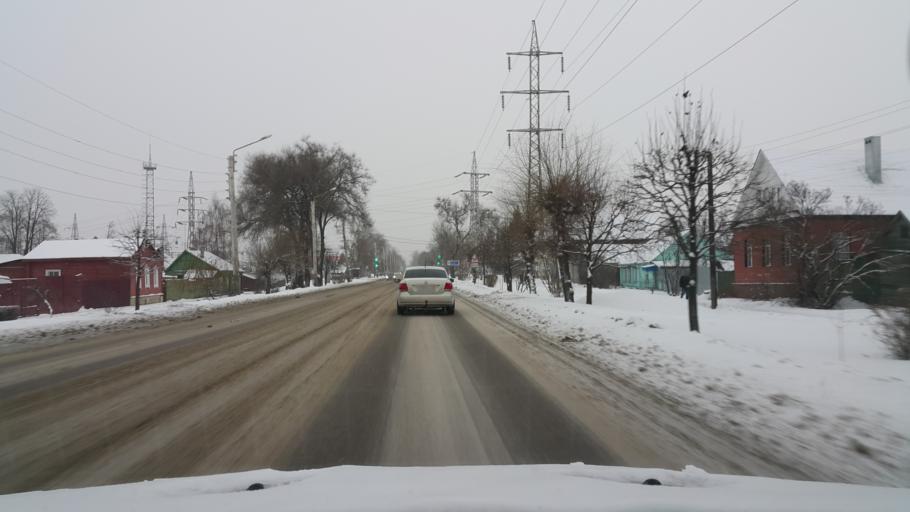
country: RU
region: Tambov
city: Pokrovo-Prigorodnoye
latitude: 52.7068
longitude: 41.4223
